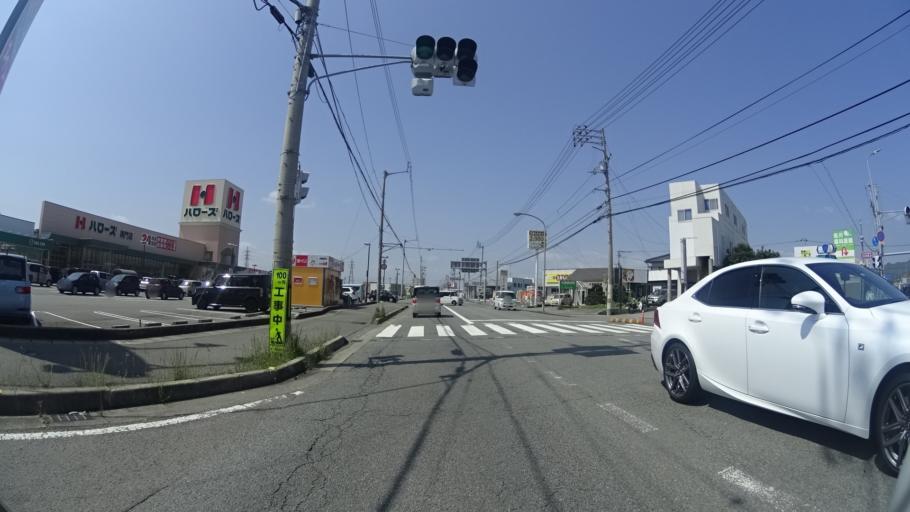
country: JP
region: Tokushima
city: Narutocho-mitsuishi
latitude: 34.1667
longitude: 134.5995
